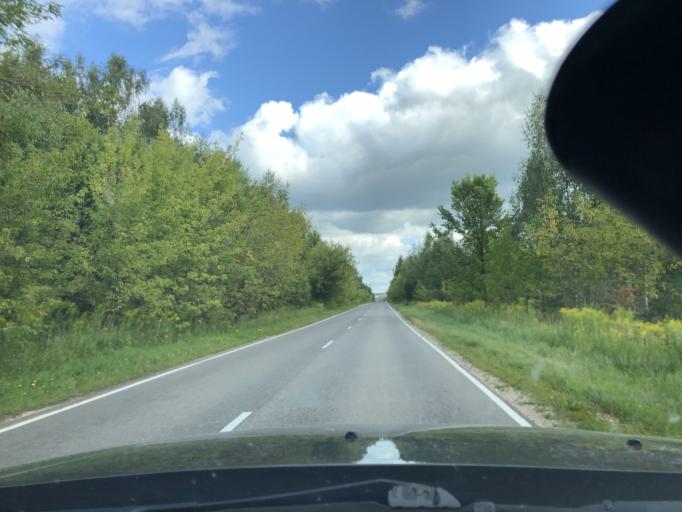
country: RU
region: Tula
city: Yasnogorsk
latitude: 54.4353
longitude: 37.6988
